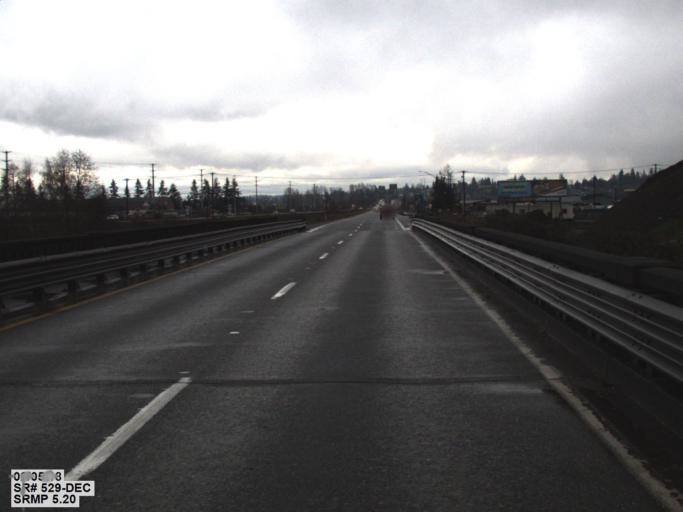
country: US
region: Washington
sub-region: Snohomish County
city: Marysville
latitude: 48.0319
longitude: -122.1836
